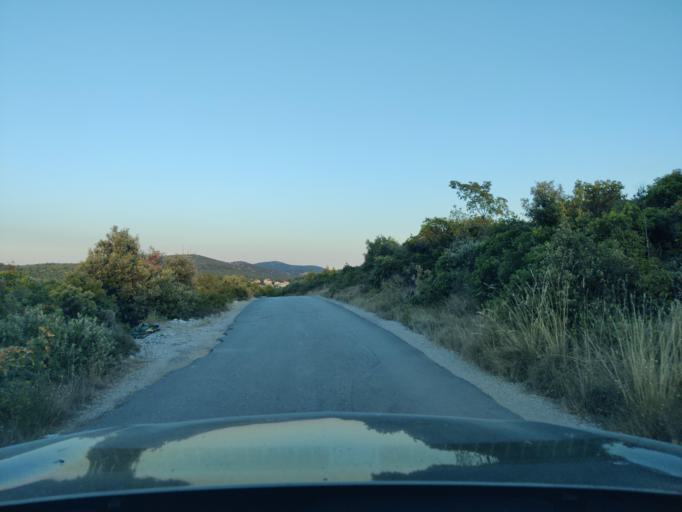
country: HR
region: Sibensko-Kniniska
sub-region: Grad Sibenik
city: Tisno
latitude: 43.8072
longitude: 15.6423
